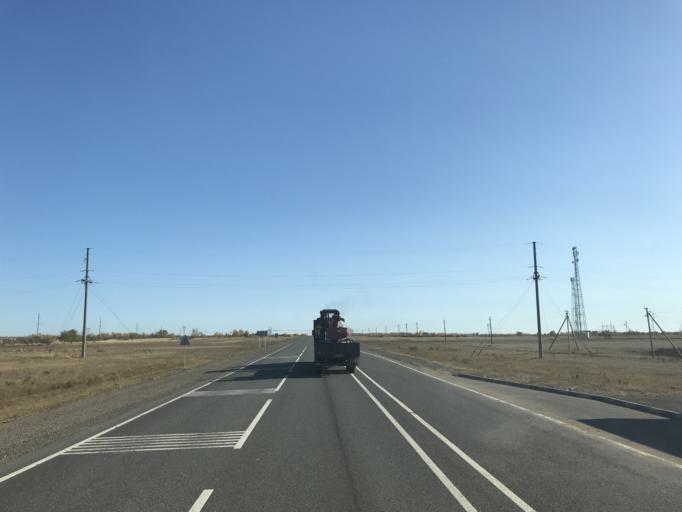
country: KZ
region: Pavlodar
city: Koktobe
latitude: 51.9242
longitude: 77.3368
